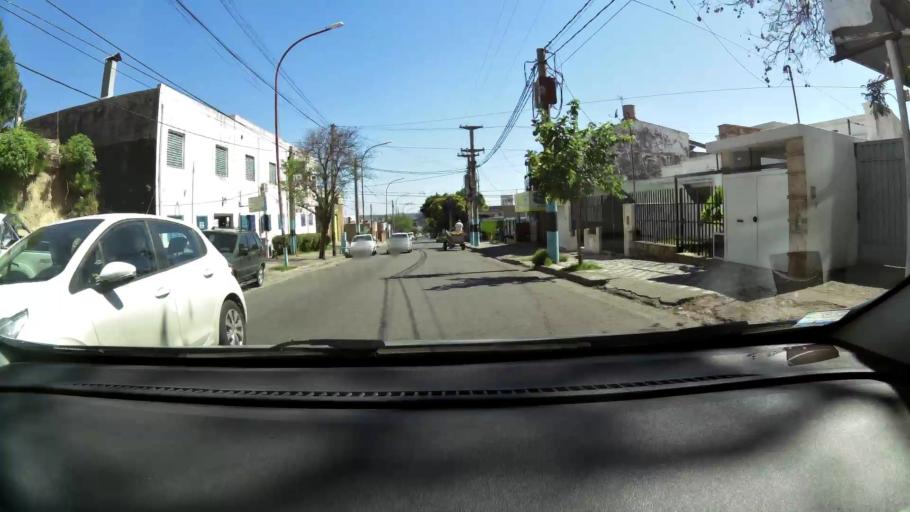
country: AR
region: Cordoba
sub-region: Departamento de Capital
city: Cordoba
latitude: -31.4318
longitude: -64.1517
